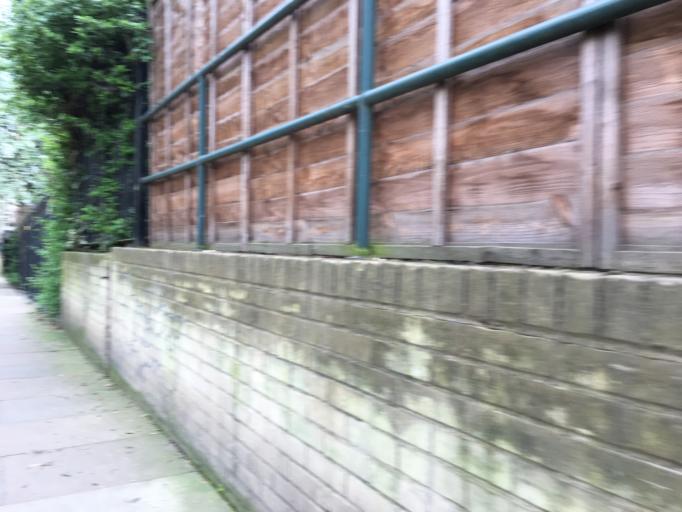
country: GB
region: England
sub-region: Greater London
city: Camden Town
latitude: 51.5516
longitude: -0.1531
